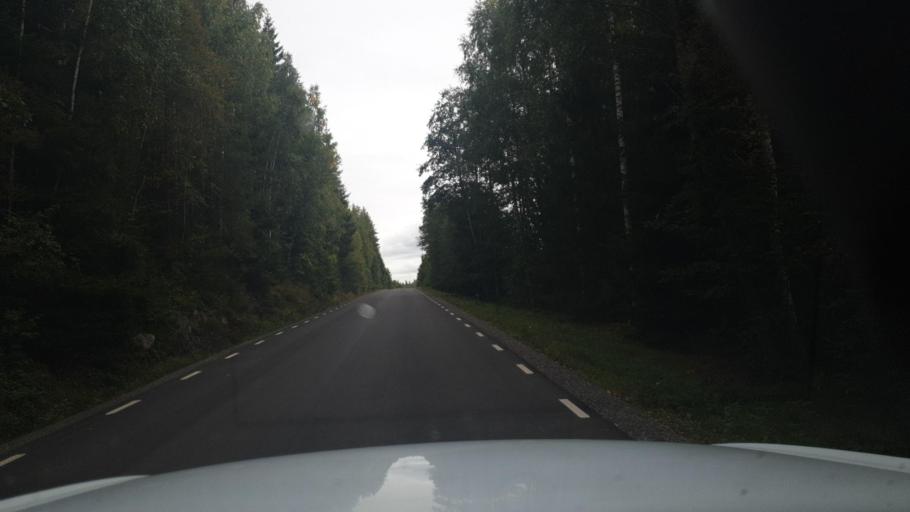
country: SE
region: Vaermland
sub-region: Torsby Kommun
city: Torsby
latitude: 59.9985
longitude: 12.7364
